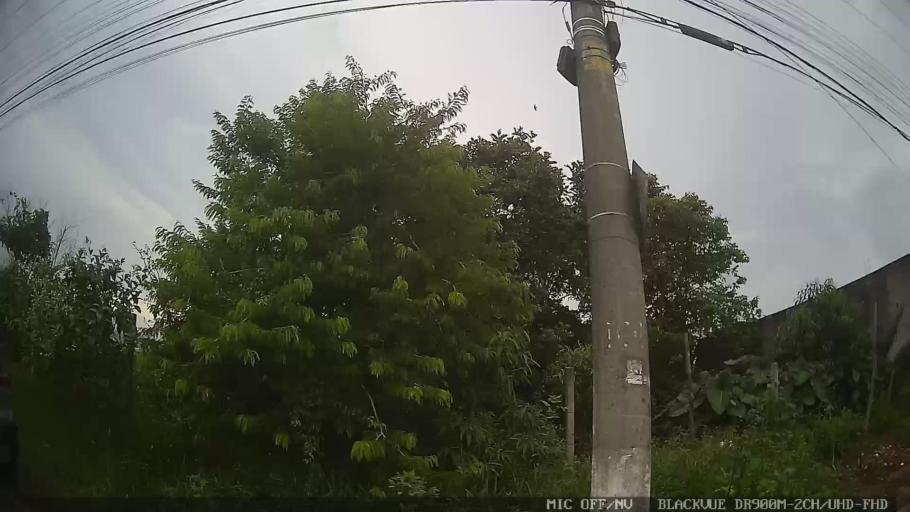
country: BR
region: Sao Paulo
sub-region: Aruja
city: Aruja
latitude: -23.4512
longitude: -46.3006
